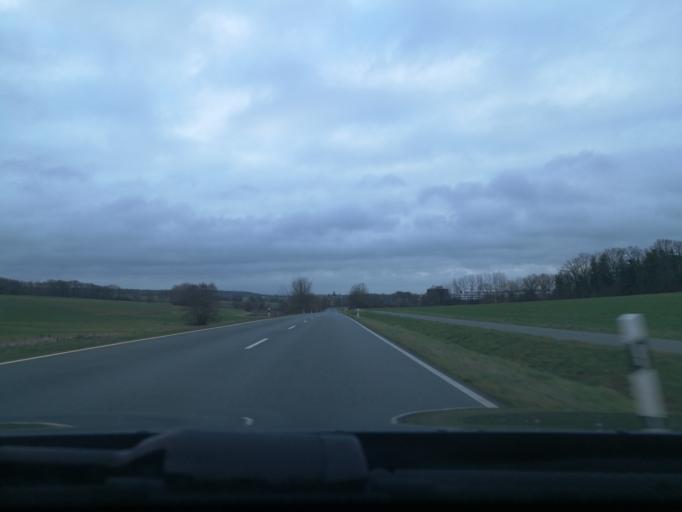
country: DE
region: Bavaria
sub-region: Regierungsbezirk Mittelfranken
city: Kalchreuth
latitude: 49.5519
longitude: 11.1439
